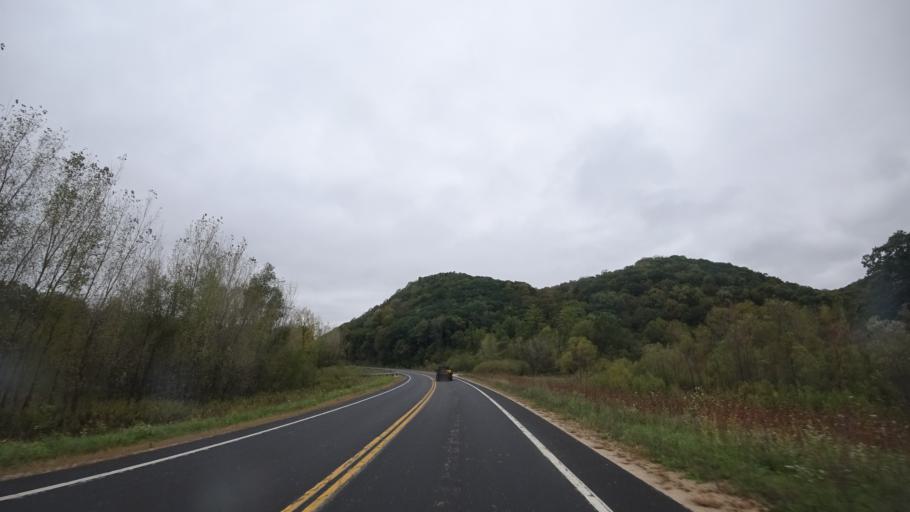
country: US
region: Wisconsin
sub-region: Grant County
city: Boscobel
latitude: 43.1450
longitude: -90.7328
